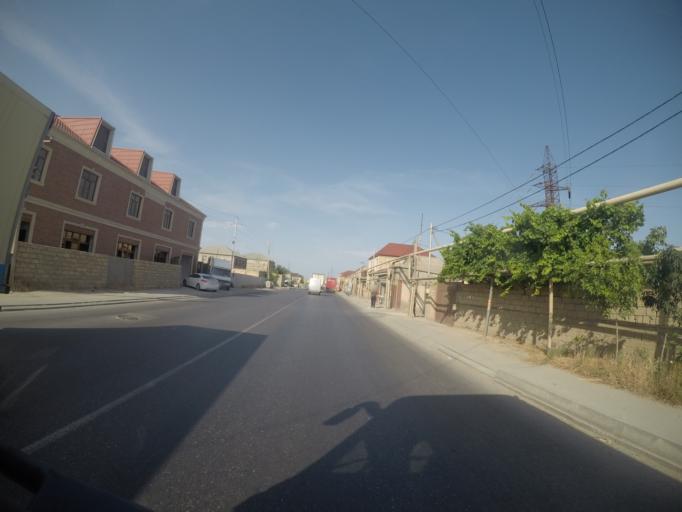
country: AZ
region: Baki
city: Bilajari
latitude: 40.4473
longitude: 49.7992
